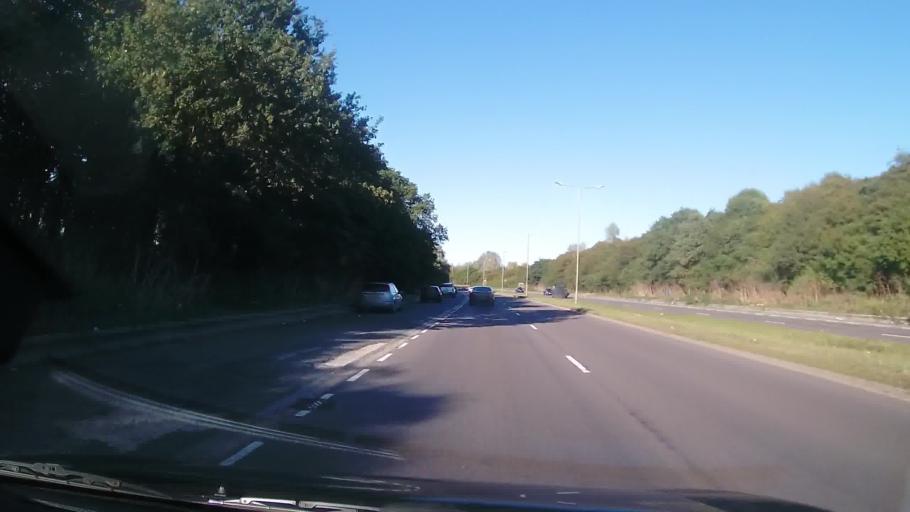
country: GB
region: England
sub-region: Buckinghamshire
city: Beaconsfield
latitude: 51.5965
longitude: -0.6260
